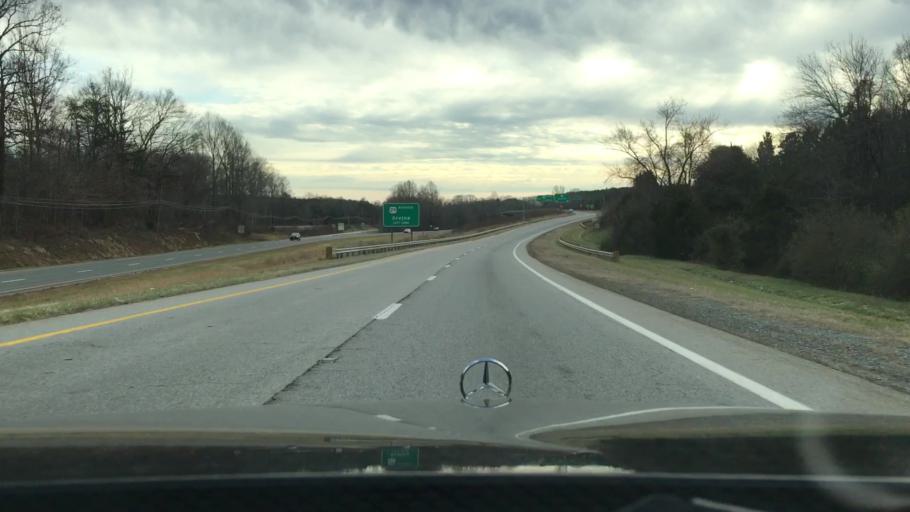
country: US
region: Virginia
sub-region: Pittsylvania County
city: Gretna
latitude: 36.9819
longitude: -79.3545
